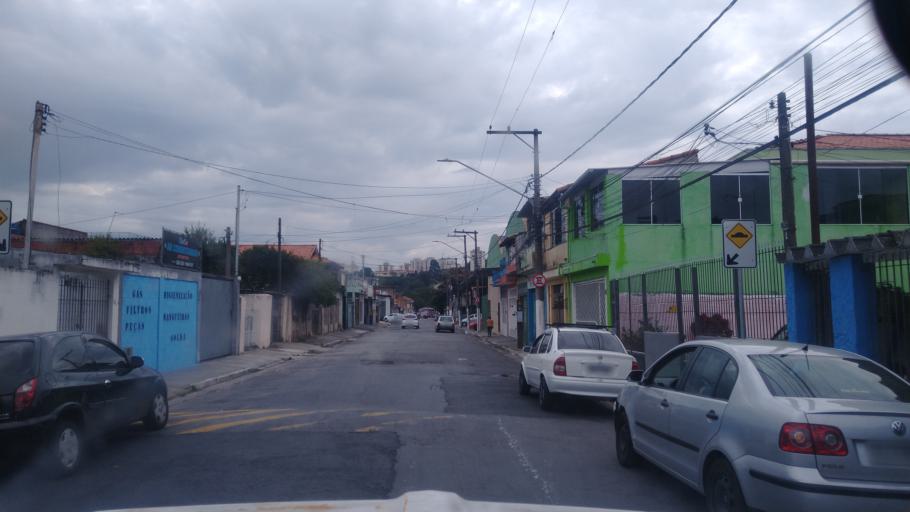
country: BR
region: Sao Paulo
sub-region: Taboao Da Serra
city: Taboao da Serra
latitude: -23.6262
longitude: -46.7616
